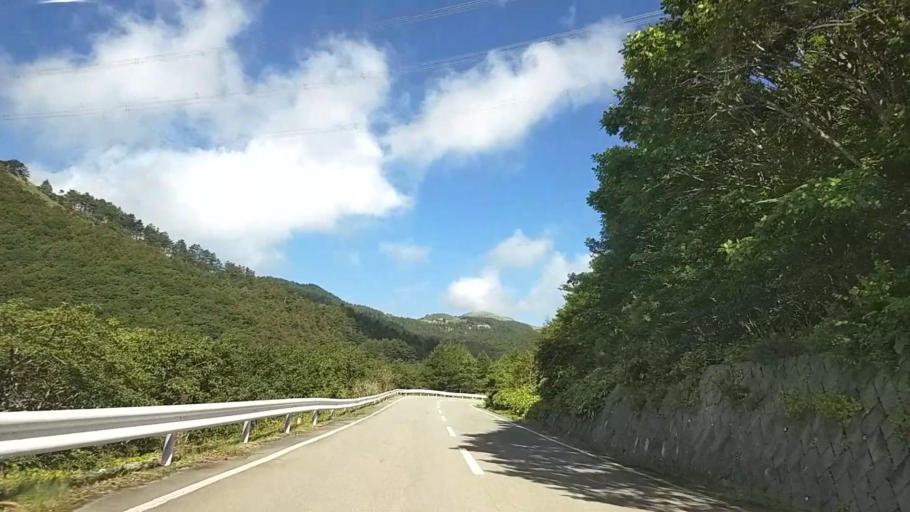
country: JP
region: Nagano
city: Suwa
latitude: 36.1421
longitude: 138.1453
